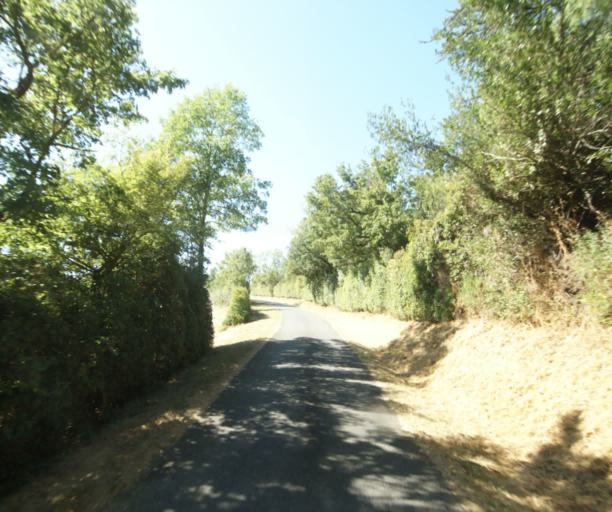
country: FR
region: Midi-Pyrenees
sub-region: Departement de la Haute-Garonne
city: Saint-Felix-Lauragais
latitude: 43.5136
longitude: 1.9301
